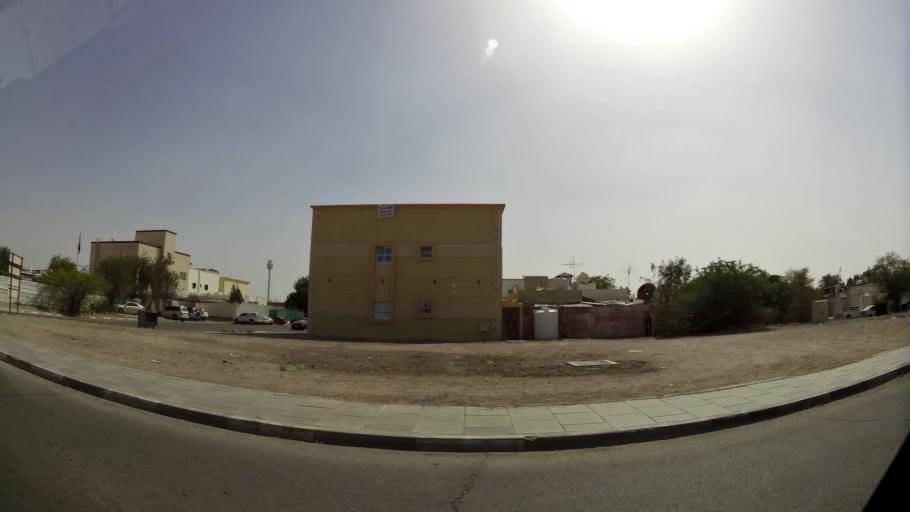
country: AE
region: Abu Dhabi
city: Al Ain
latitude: 24.2380
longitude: 55.6988
